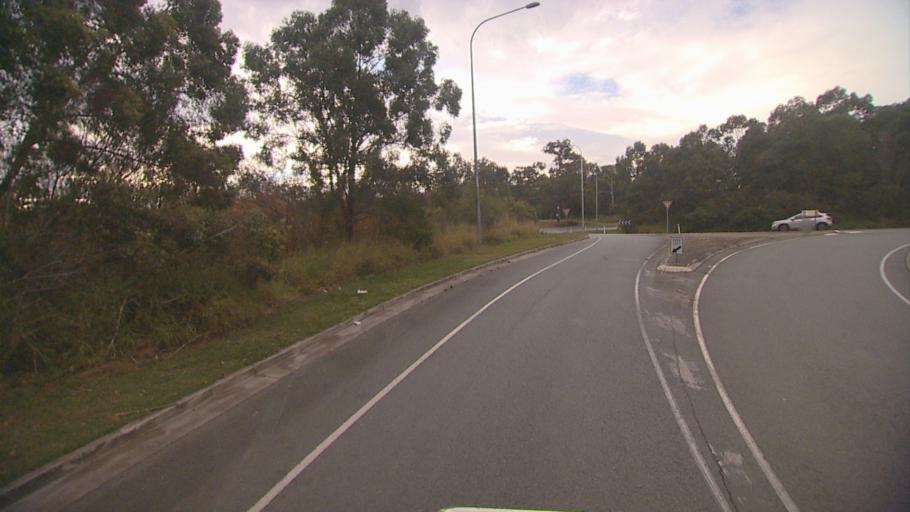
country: AU
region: Queensland
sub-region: Logan
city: Park Ridge South
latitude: -27.7260
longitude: 153.0288
